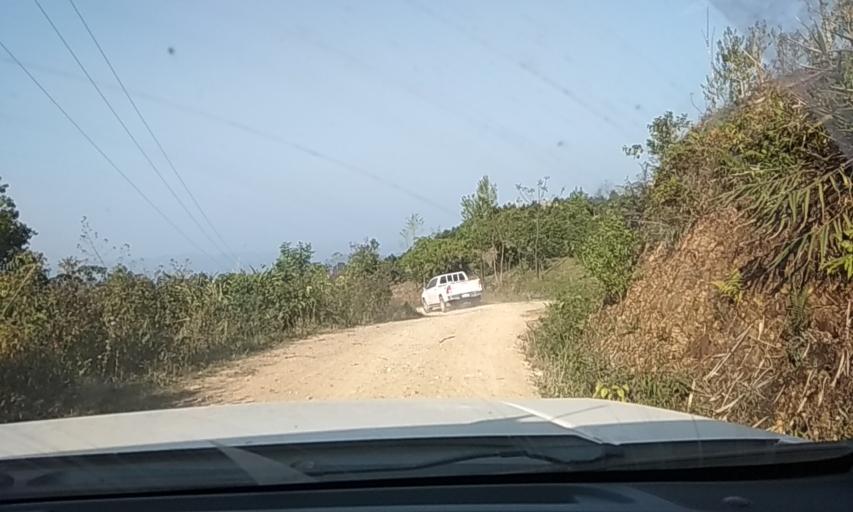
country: LA
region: Phongsali
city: Phongsali
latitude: 21.6601
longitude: 102.1744
